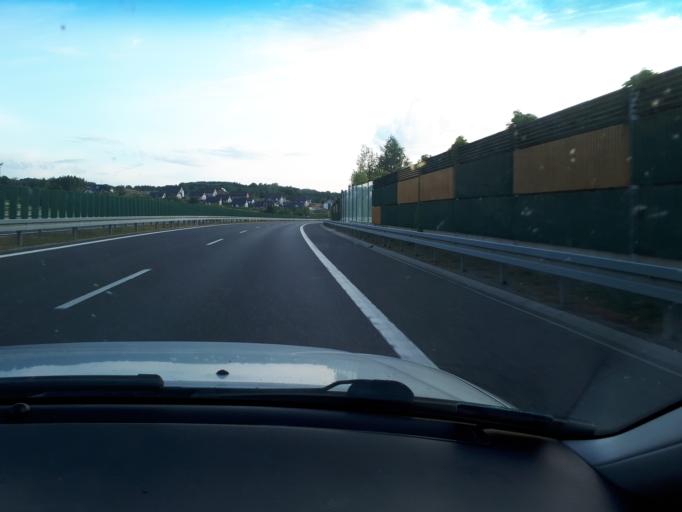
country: PL
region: Subcarpathian Voivodeship
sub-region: Powiat ropczycko-sedziszowski
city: Ropczyce
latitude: 50.0514
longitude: 21.6244
